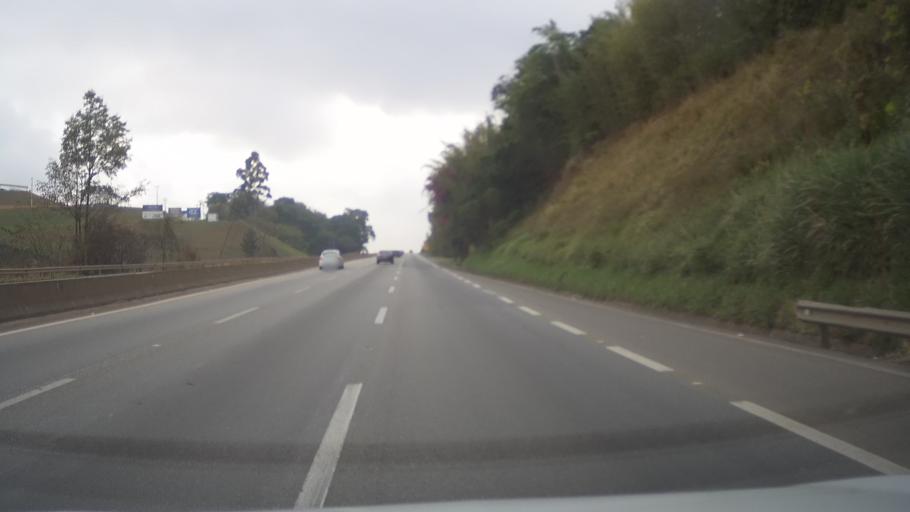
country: BR
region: Minas Gerais
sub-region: Extrema
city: Extrema
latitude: -22.8695
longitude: -46.3565
